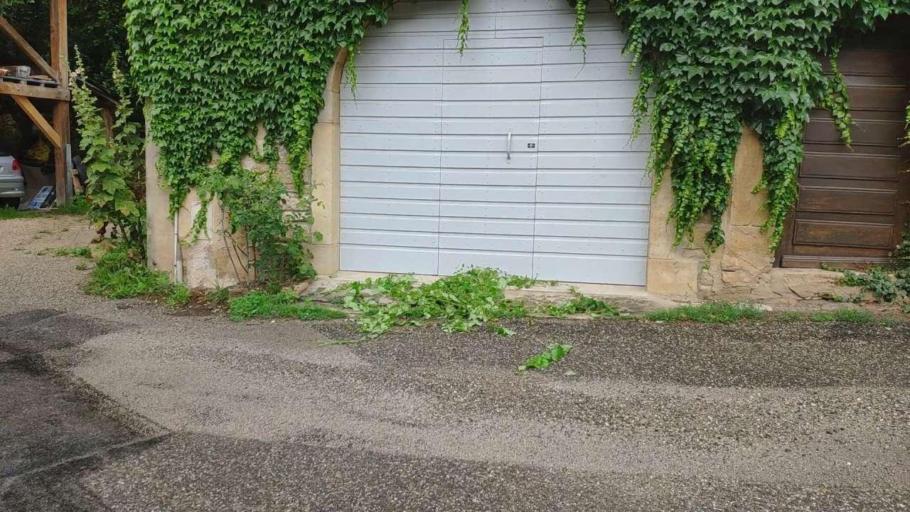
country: FR
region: Franche-Comte
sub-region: Departement du Jura
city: Poligny
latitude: 46.7834
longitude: 5.6162
